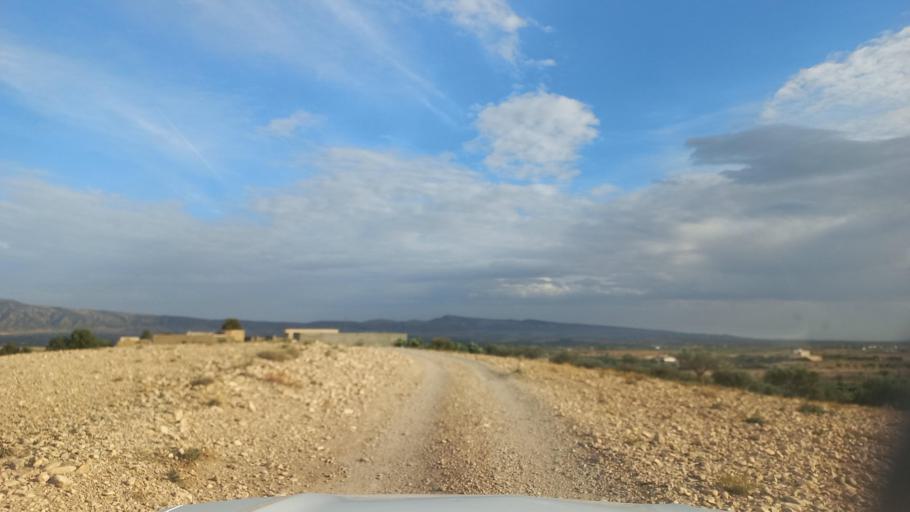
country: TN
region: Al Qasrayn
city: Sbiba
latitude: 35.4555
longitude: 9.0838
